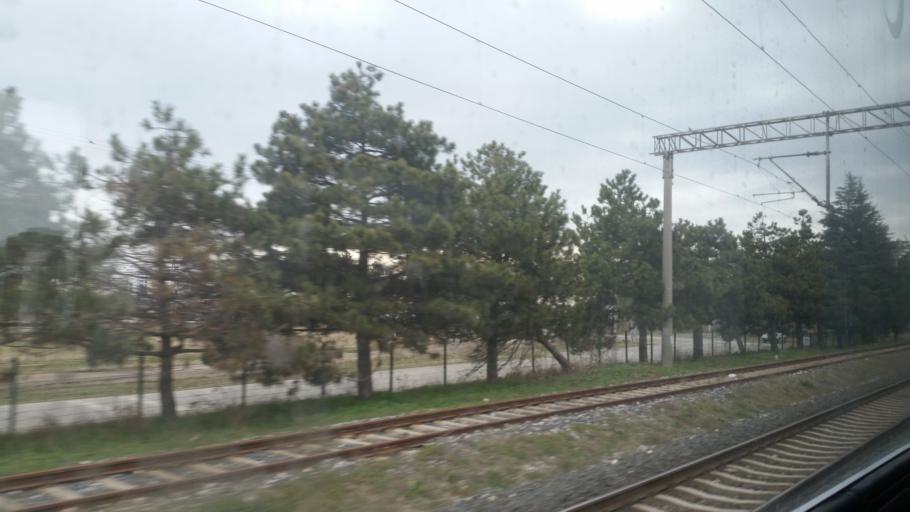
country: TR
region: Tekirdag
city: Velimese
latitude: 41.2446
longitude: 27.8843
